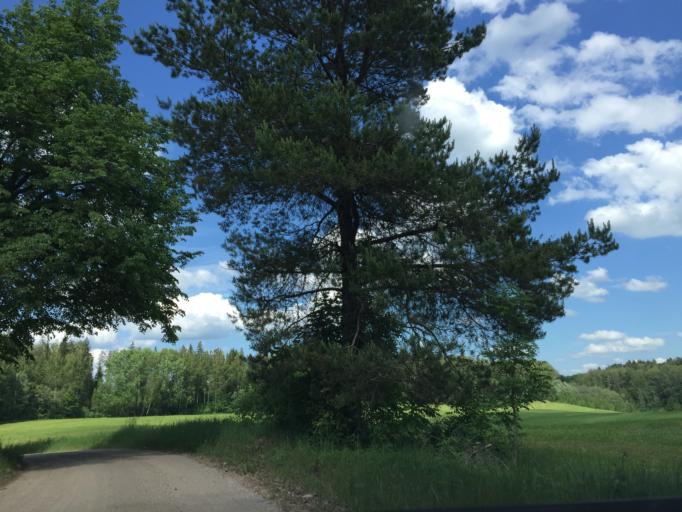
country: LV
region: Priekuli
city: Priekuli
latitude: 57.2397
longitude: 25.4165
